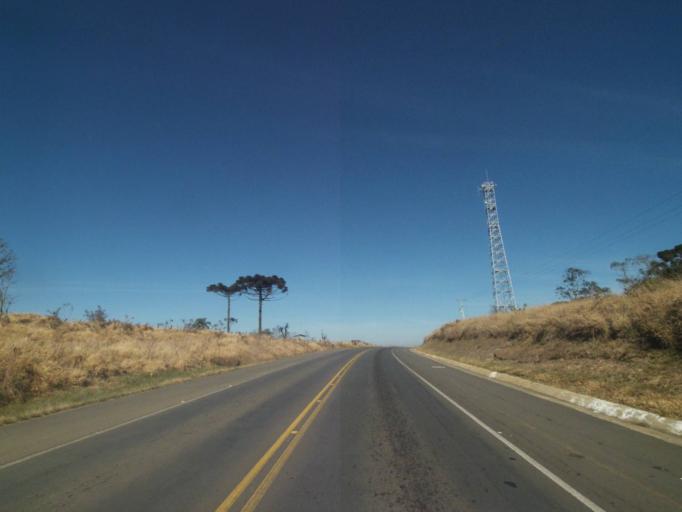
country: BR
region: Parana
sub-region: Tibagi
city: Tibagi
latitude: -24.7991
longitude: -50.4672
